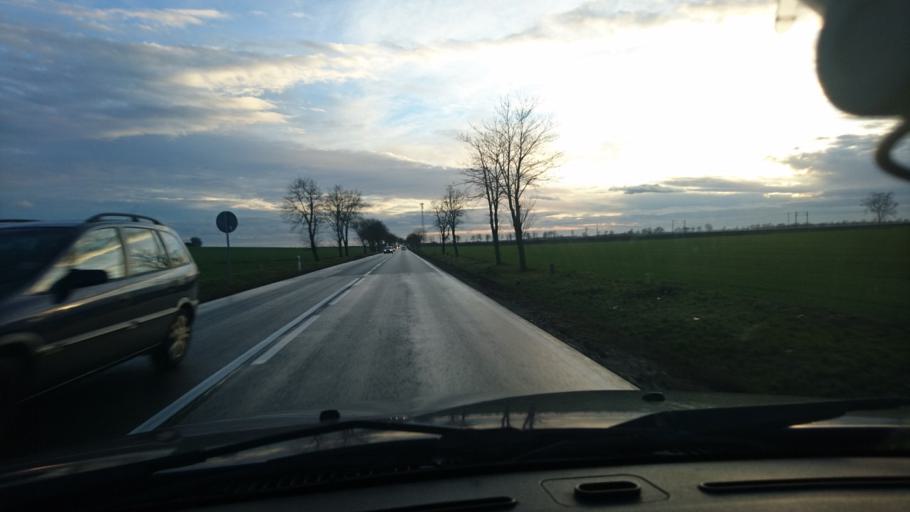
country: PL
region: Opole Voivodeship
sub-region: Powiat kluczborski
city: Byczyna
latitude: 51.1039
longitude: 18.2061
